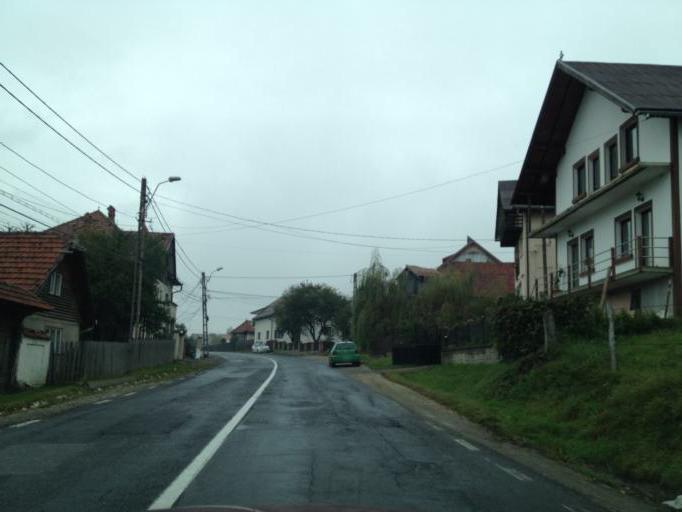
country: RO
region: Brasov
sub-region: Comuna Moeciu
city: Moieciu de Jos
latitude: 45.4957
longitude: 25.3259
